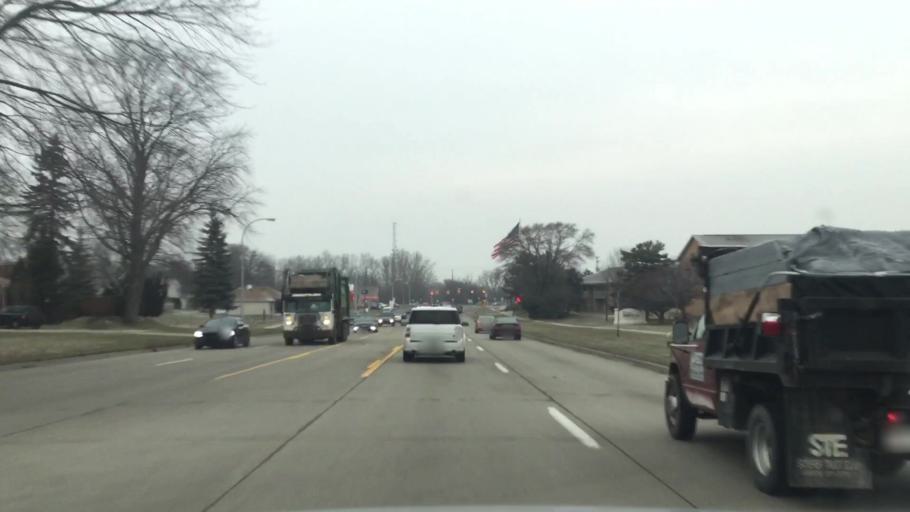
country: US
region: Michigan
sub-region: Wayne County
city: Garden City
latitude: 42.3360
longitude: -83.3508
